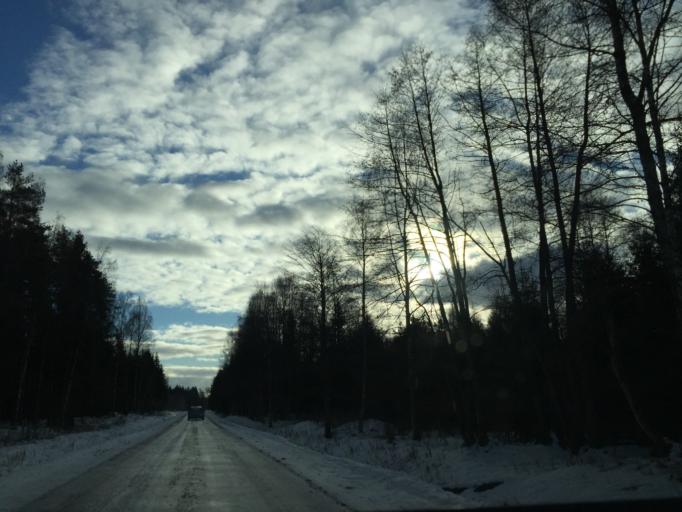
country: LV
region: Ogre
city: Jumprava
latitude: 56.5525
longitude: 24.8576
